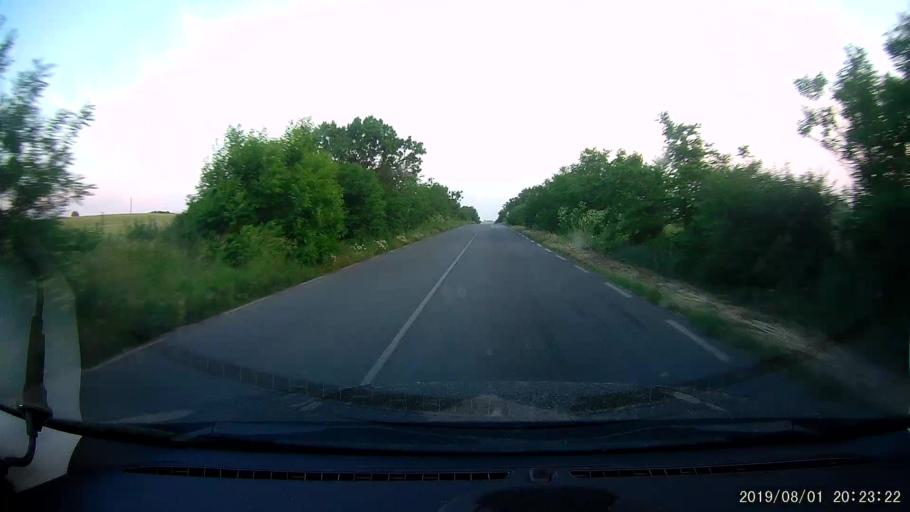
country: BG
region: Yambol
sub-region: Obshtina Elkhovo
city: Elkhovo
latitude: 42.2500
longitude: 26.5988
